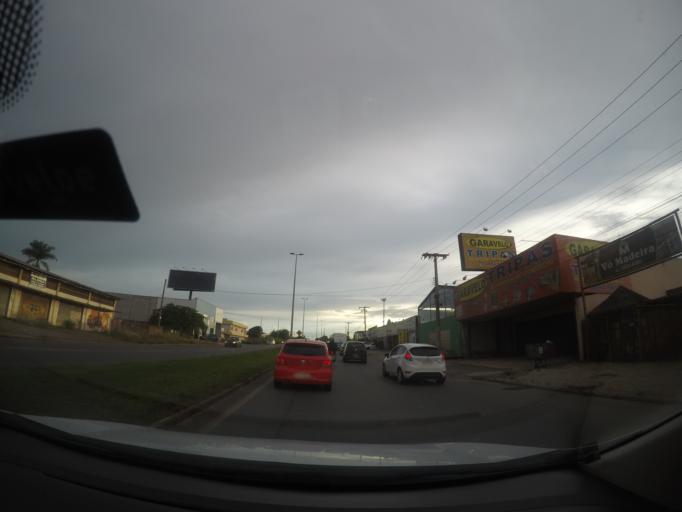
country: BR
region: Goias
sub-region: Goiania
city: Goiania
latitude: -16.7498
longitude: -49.3329
